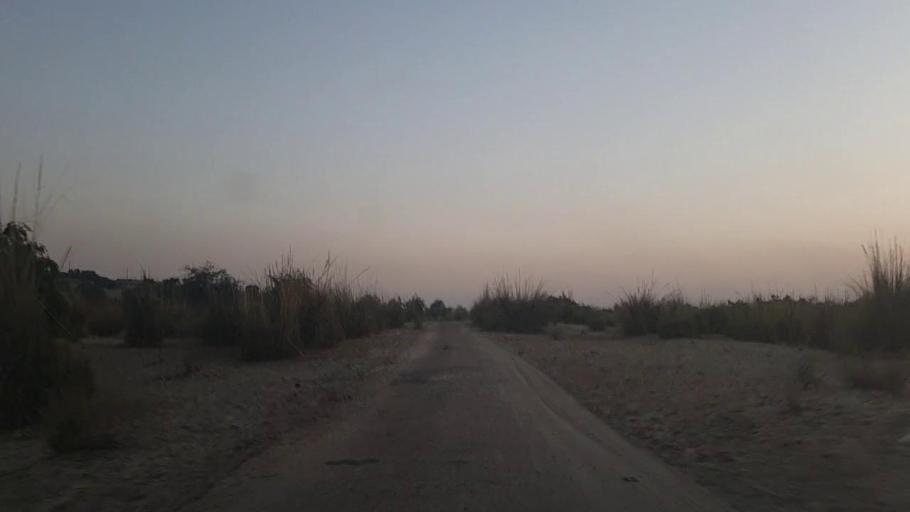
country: PK
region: Sindh
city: Jam Sahib
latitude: 26.3931
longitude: 68.8095
